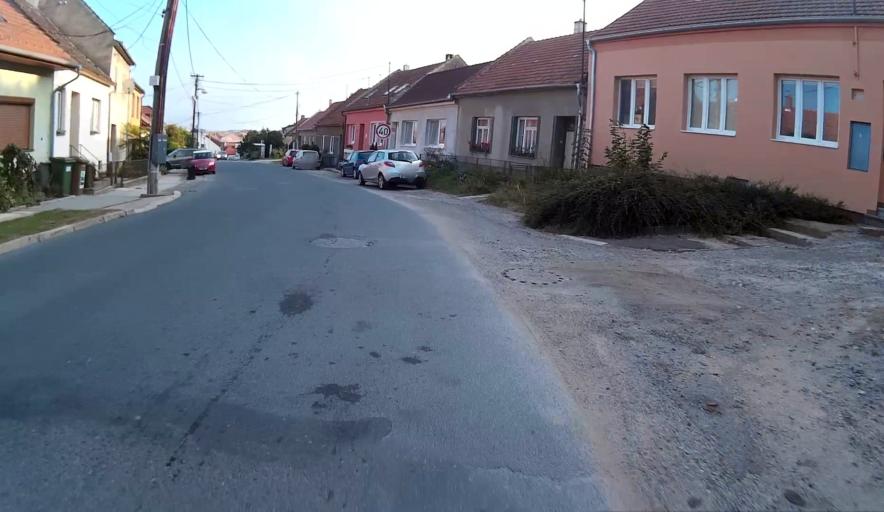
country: CZ
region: South Moravian
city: Podoli
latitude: 49.1924
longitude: 16.7196
